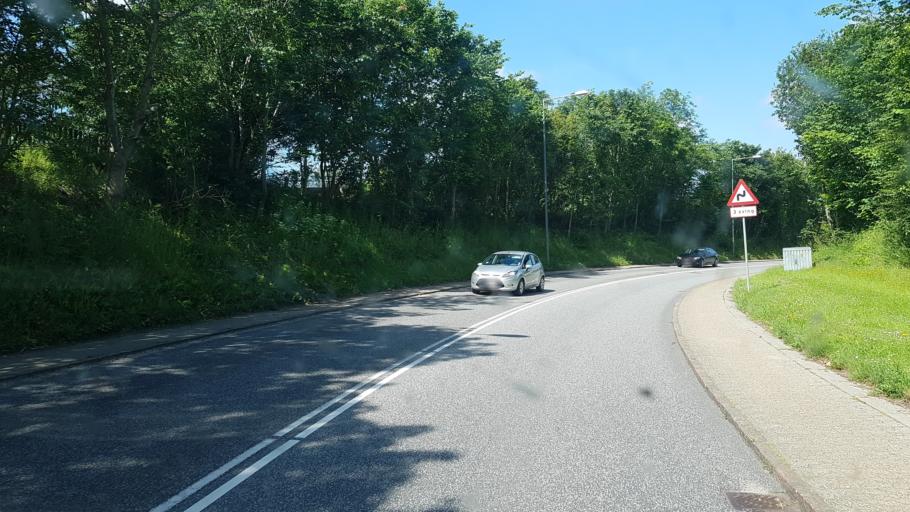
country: DK
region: Central Jutland
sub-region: Lemvig Kommune
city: Lemvig
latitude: 56.5486
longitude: 8.3205
